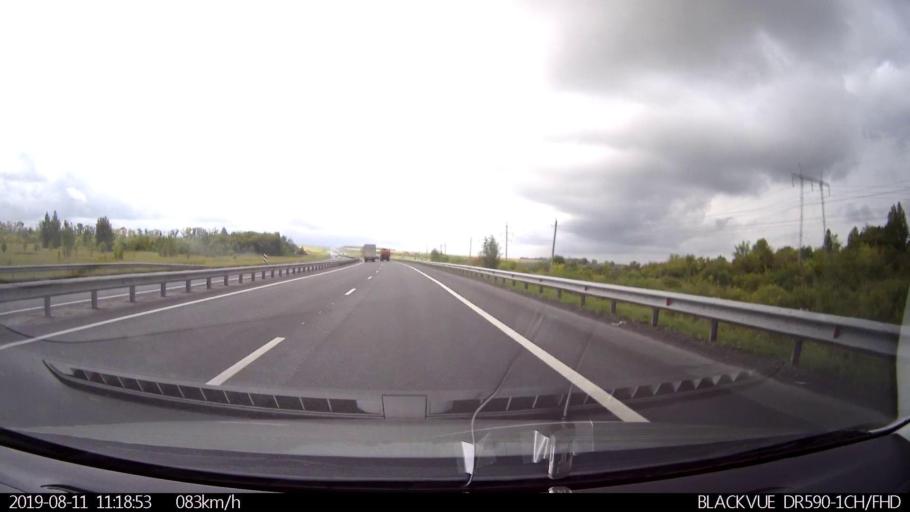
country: RU
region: Ulyanovsk
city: Novoul'yanovsk
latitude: 54.1755
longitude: 48.2652
